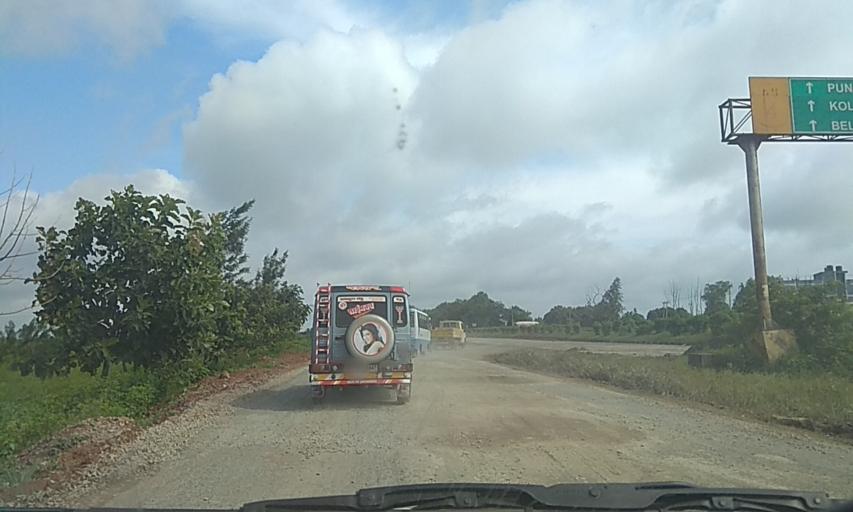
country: IN
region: Karnataka
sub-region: Haveri
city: Shiggaon
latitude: 15.0434
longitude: 75.1709
